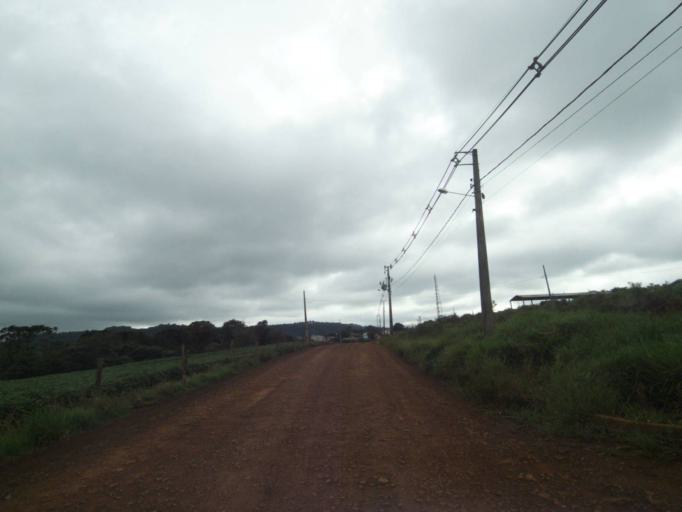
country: BR
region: Parana
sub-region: Pitanga
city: Pitanga
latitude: -24.9406
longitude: -51.8769
